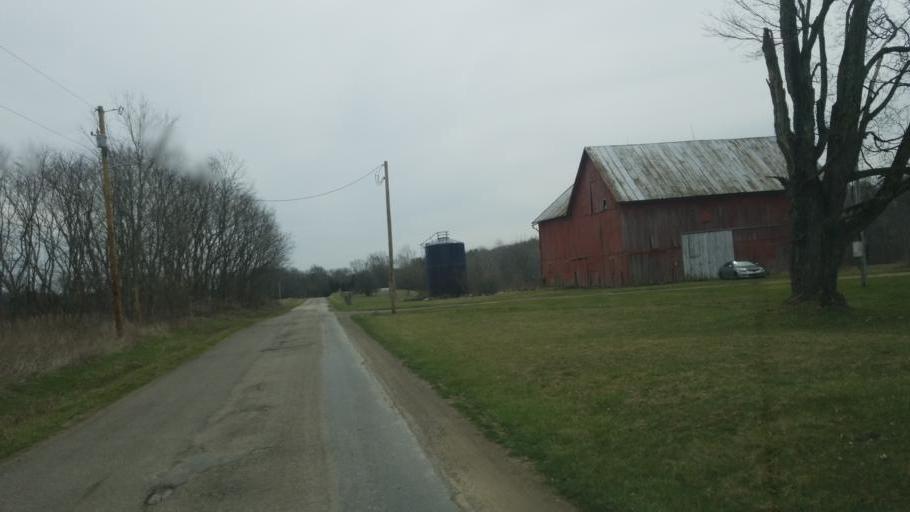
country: US
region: Ohio
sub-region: Knox County
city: Centerburg
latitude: 40.3545
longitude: -82.6412
